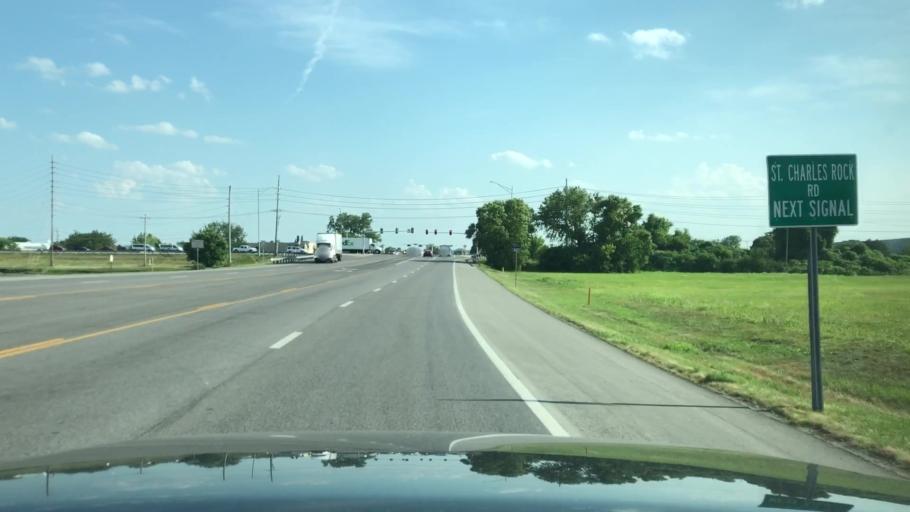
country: US
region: Missouri
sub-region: Saint Charles County
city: Saint Charles
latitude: 38.7810
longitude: -90.4591
